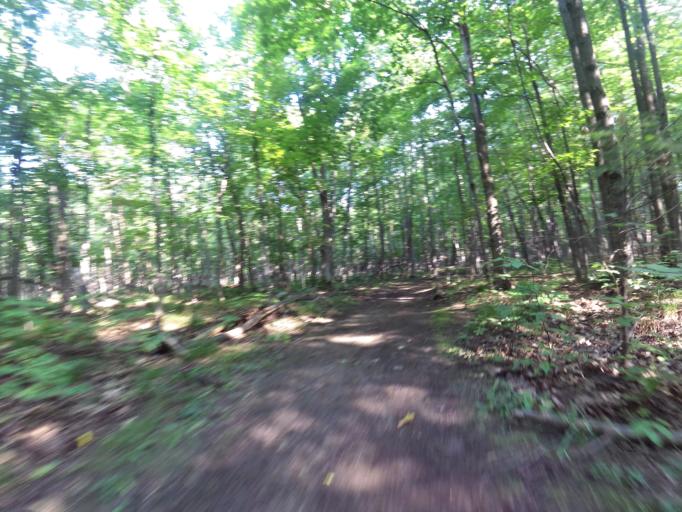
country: CA
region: Ontario
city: Bells Corners
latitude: 45.2940
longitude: -75.8434
